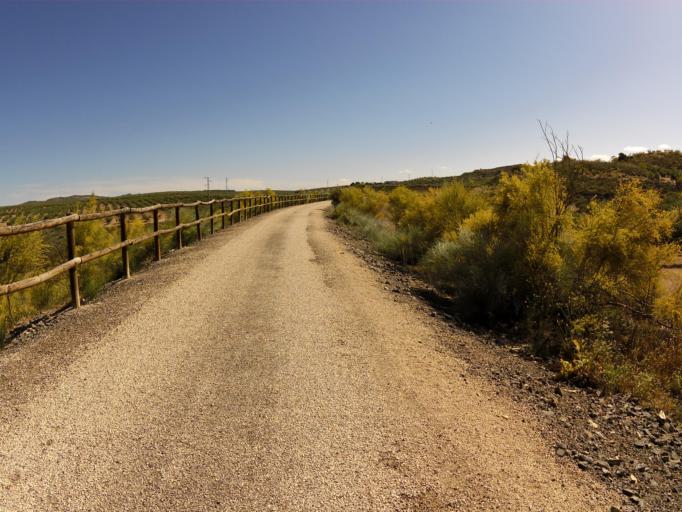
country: ES
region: Andalusia
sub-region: Provincia de Jaen
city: Alcaudete
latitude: 37.6043
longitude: -4.1583
